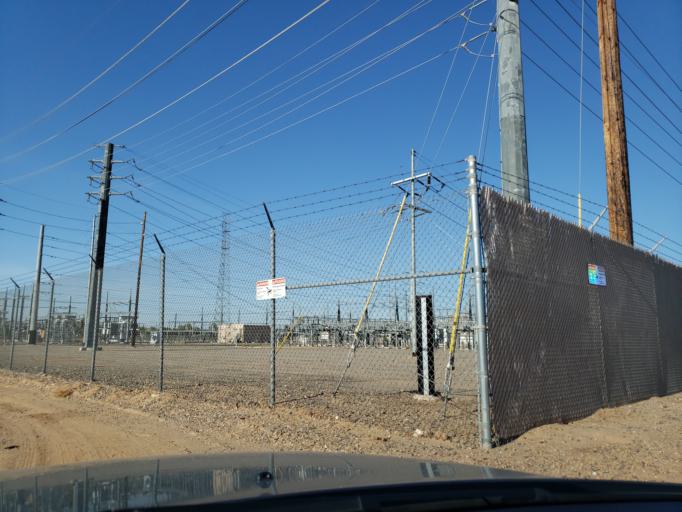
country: US
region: Arizona
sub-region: Maricopa County
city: Avondale
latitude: 33.4676
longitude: -112.3120
